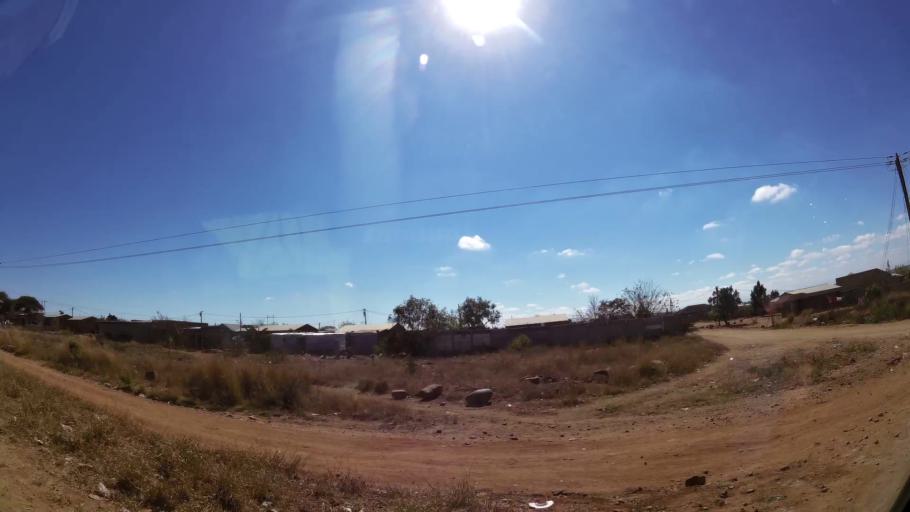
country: ZA
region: Limpopo
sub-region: Capricorn District Municipality
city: Polokwane
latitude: -23.8896
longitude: 29.4064
